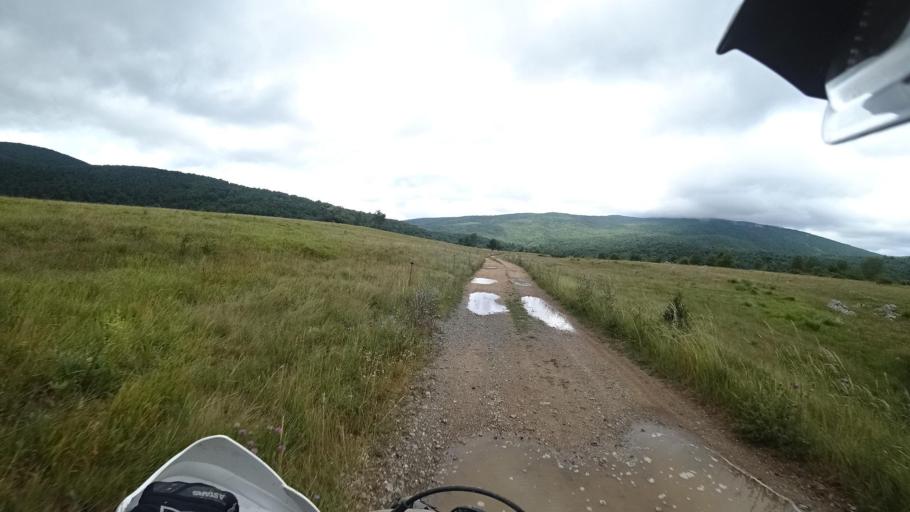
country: HR
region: Licko-Senjska
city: Jezerce
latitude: 44.7806
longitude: 15.4962
